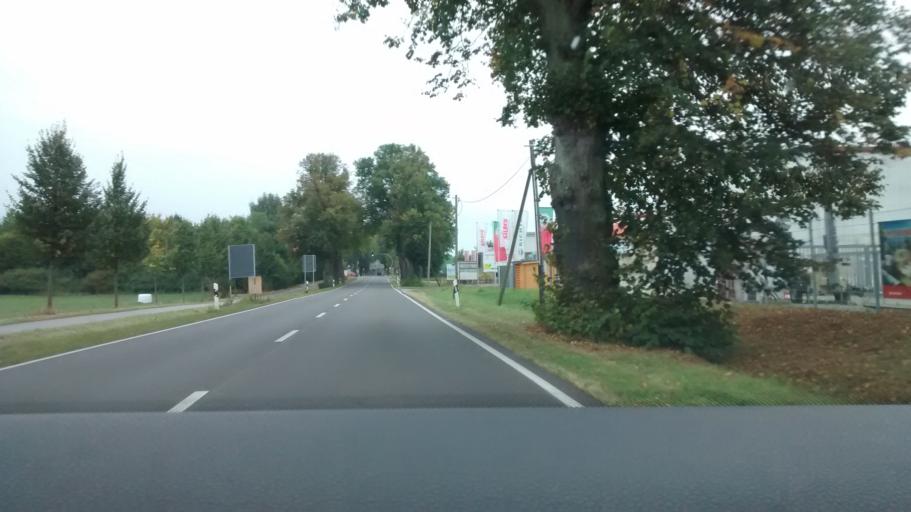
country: DE
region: Mecklenburg-Vorpommern
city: Wismar
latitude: 53.8676
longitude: 11.4507
